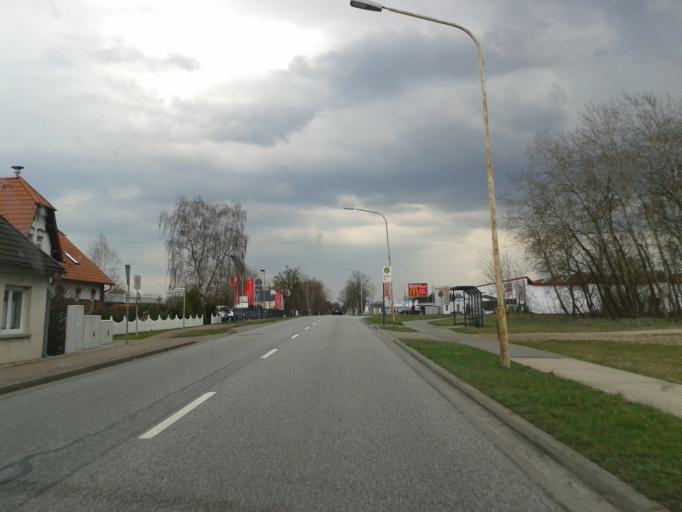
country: DE
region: Saxony-Anhalt
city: Salzwedel
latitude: 52.8683
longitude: 11.0910
